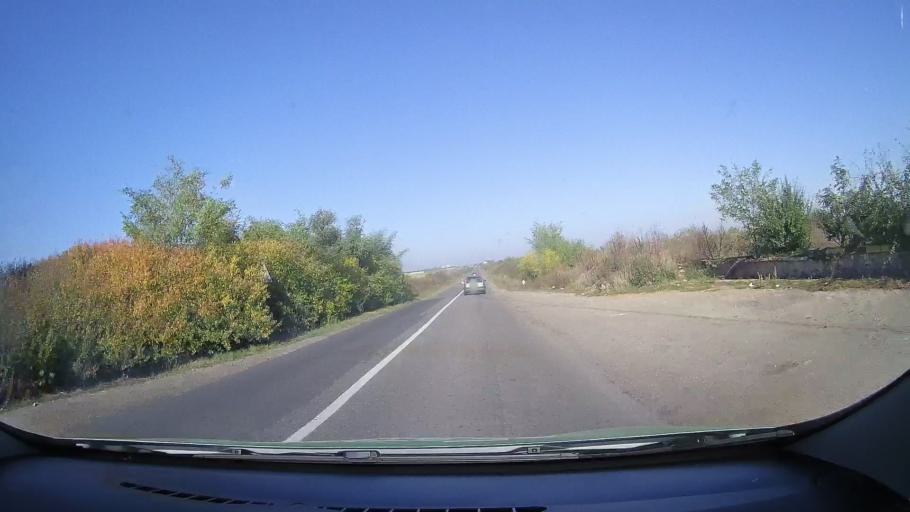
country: RO
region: Satu Mare
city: Carei
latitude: 47.6627
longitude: 22.4926
